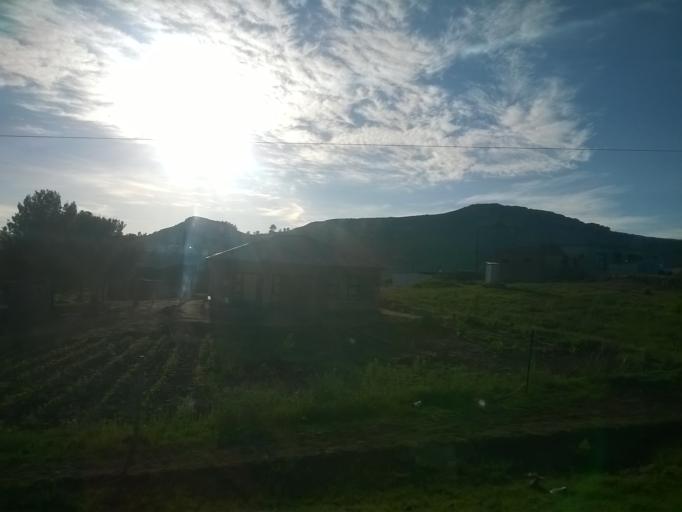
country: LS
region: Maseru
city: Maseru
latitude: -29.2406
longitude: 27.6062
